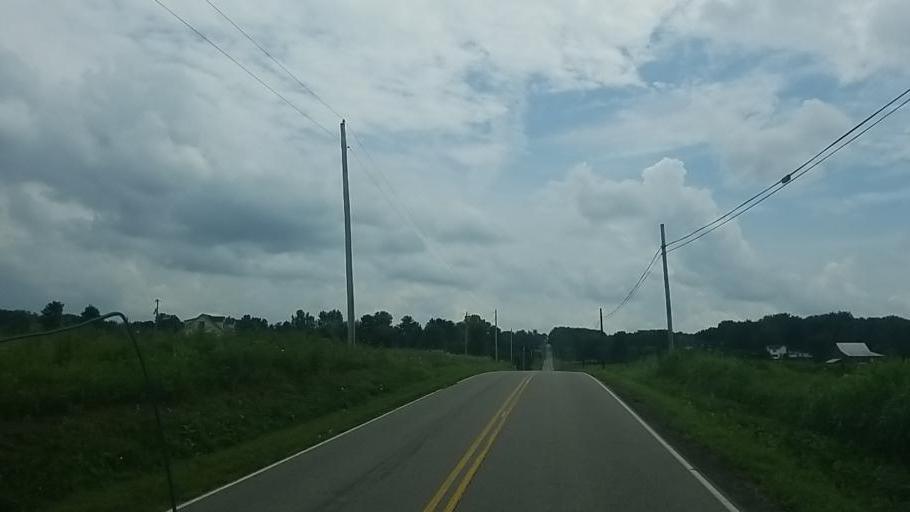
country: US
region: Ohio
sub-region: Licking County
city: Utica
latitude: 40.2289
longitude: -82.3654
